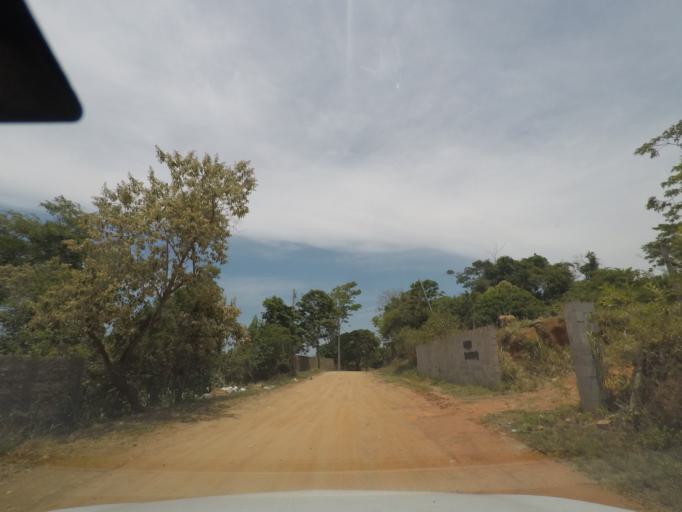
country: BR
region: Rio de Janeiro
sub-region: Marica
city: Marica
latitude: -22.9255
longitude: -42.8262
